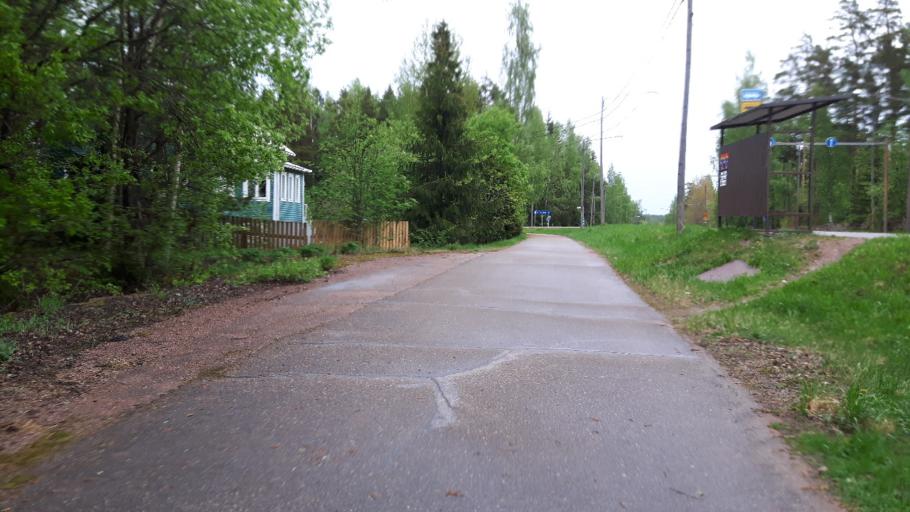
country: FI
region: Kymenlaakso
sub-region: Kotka-Hamina
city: Karhula
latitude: 60.5549
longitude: 26.9897
